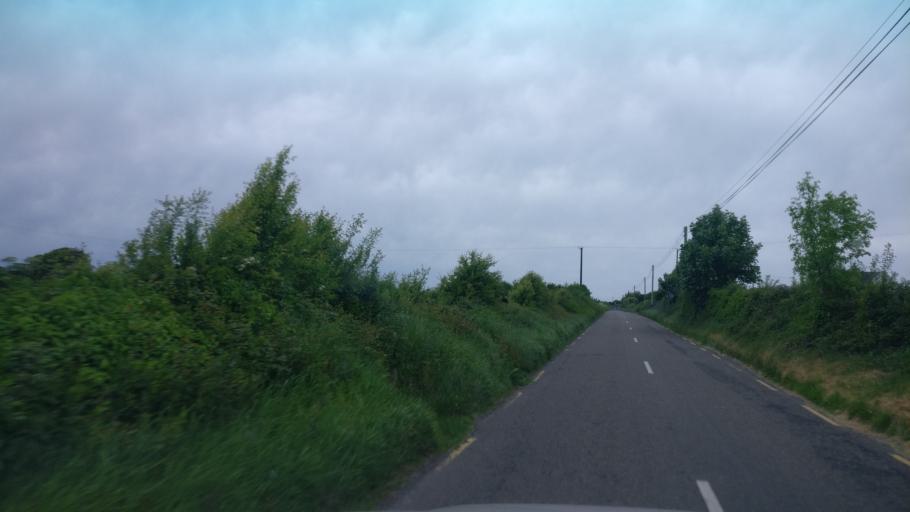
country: IE
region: Connaught
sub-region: County Galway
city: Portumna
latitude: 53.1086
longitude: -8.2674
